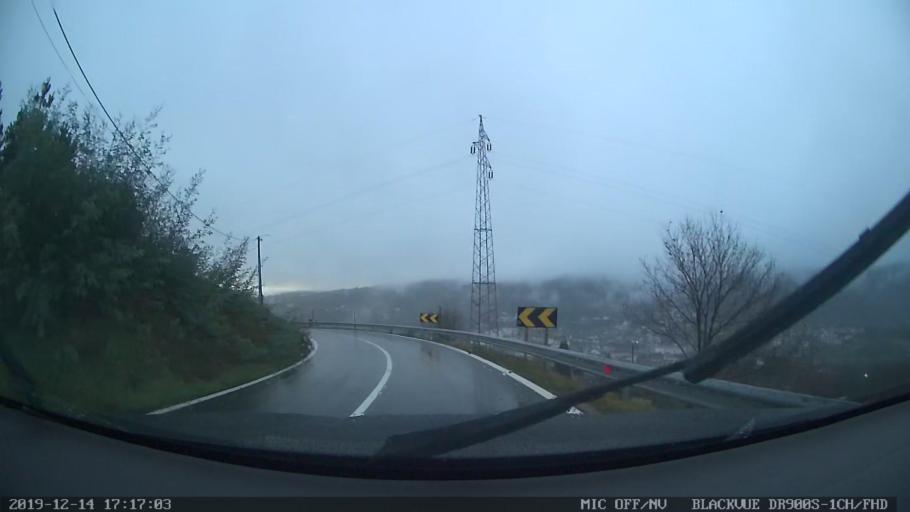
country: PT
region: Vila Real
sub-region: Vila Pouca de Aguiar
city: Vila Pouca de Aguiar
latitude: 41.5005
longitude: -7.6361
